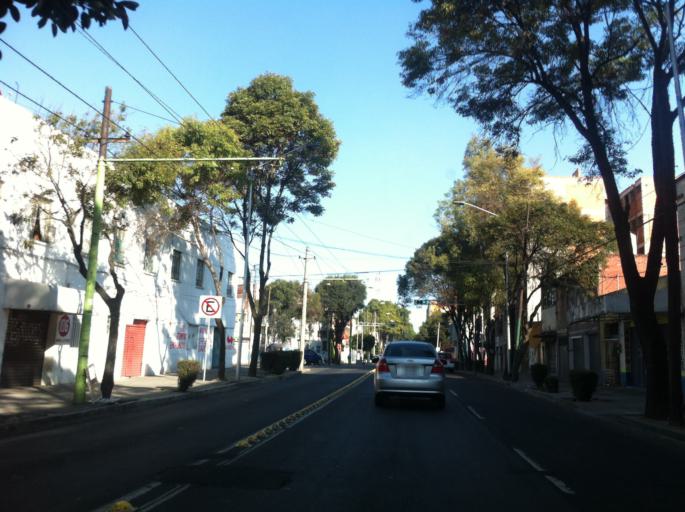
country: MX
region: Mexico City
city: Mexico City
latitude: 19.4148
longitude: -99.1384
